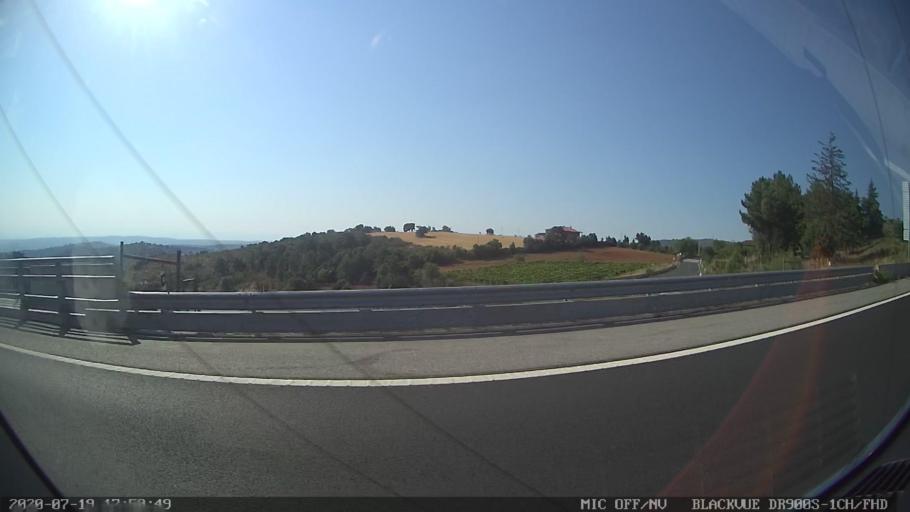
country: PT
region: Braganca
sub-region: Macedo de Cavaleiros
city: Macedo de Cavaleiros
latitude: 41.5647
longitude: -7.0099
